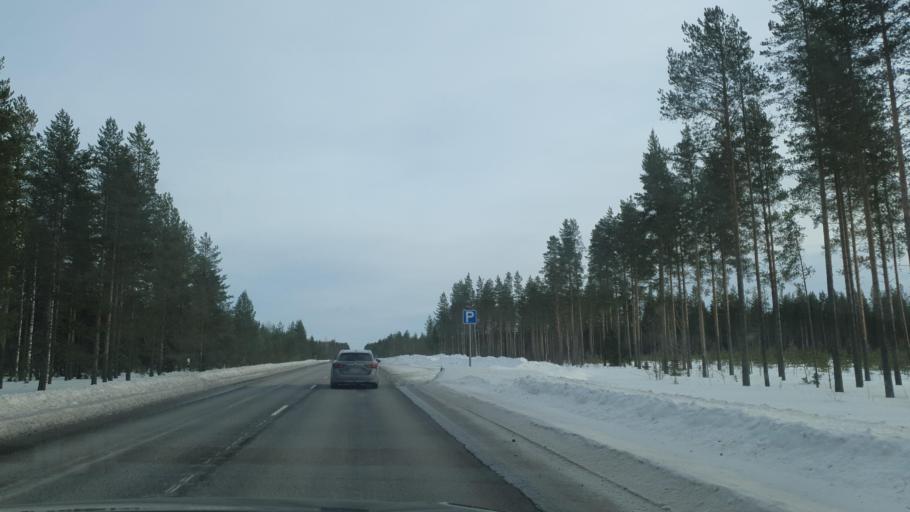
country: FI
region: Kainuu
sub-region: Kajaani
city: Vaala
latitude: 64.5542
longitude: 27.0444
